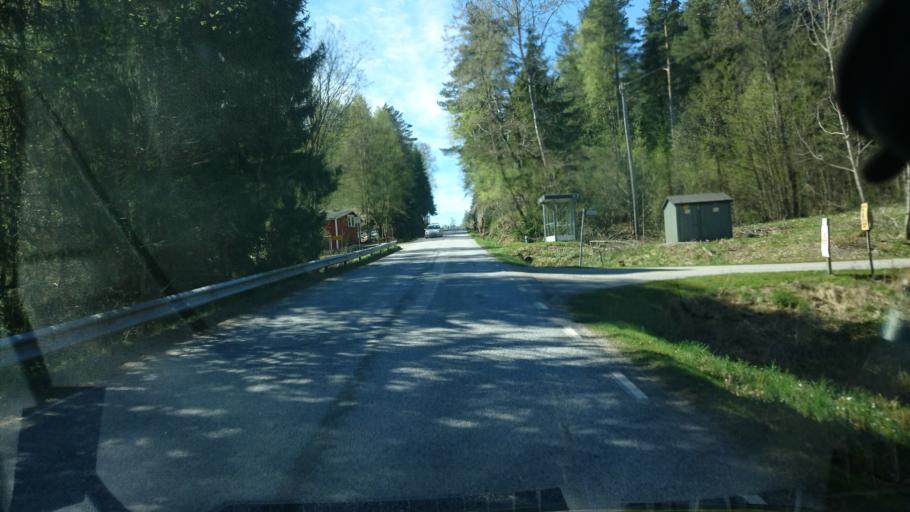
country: SE
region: Vaestra Goetaland
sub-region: Munkedals Kommun
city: Munkedal
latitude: 58.4218
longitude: 11.6918
